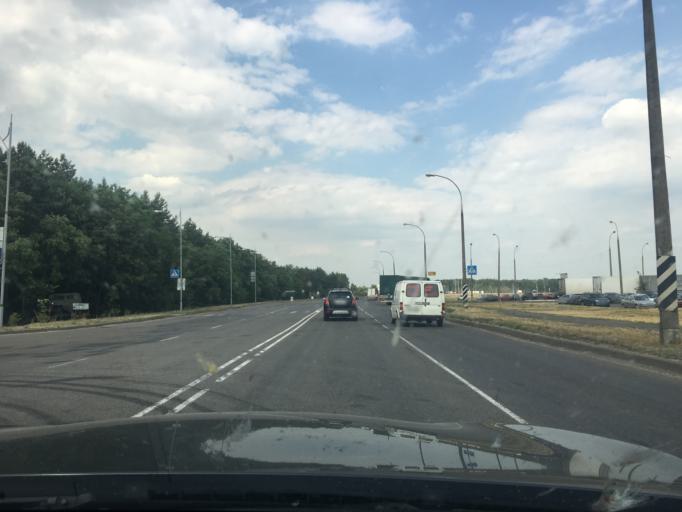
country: BY
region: Brest
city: Brest
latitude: 52.1478
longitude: 23.6864
